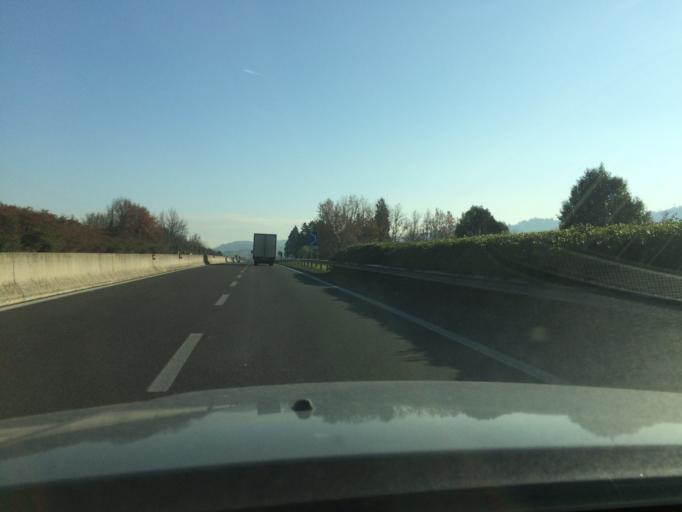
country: IT
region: Umbria
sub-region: Provincia di Perugia
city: Ponterio-Pian di Porto
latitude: 42.7960
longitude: 12.4163
